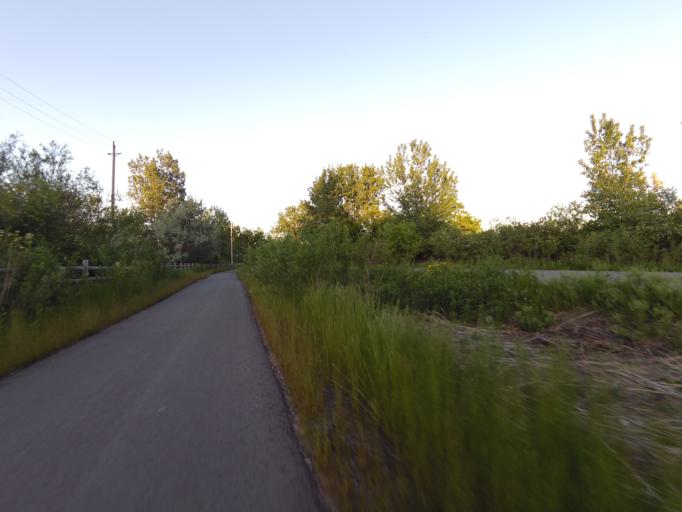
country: CA
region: Ontario
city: Toronto
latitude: 43.6472
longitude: -79.3260
